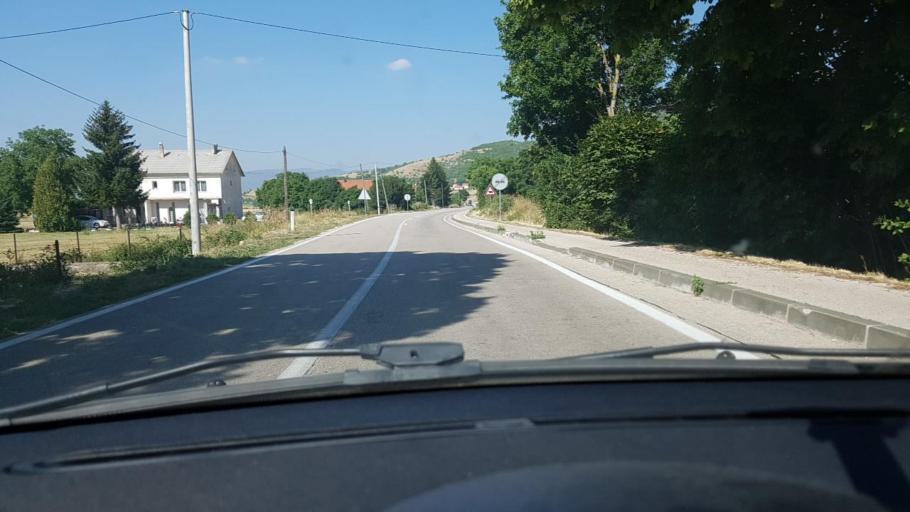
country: BA
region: Federation of Bosnia and Herzegovina
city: Zabrisce
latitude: 43.8704
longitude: 16.9213
